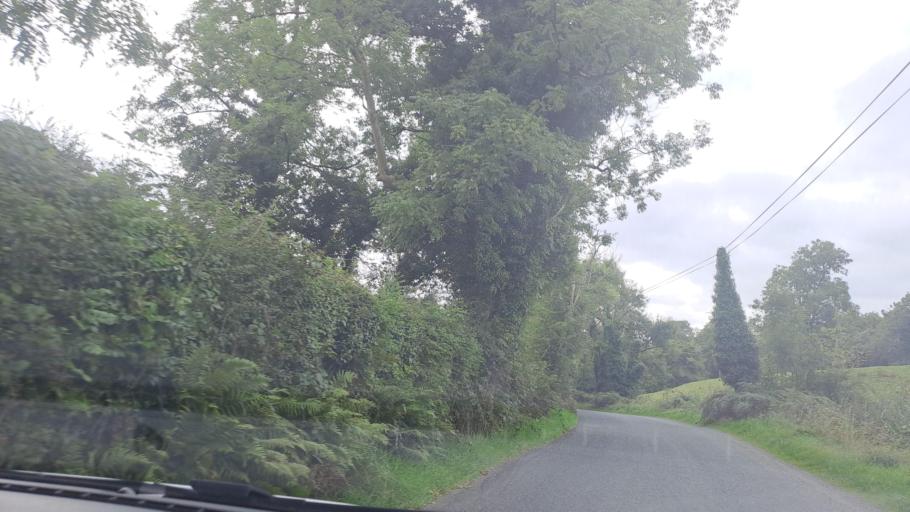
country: IE
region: Ulster
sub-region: An Cabhan
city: Bailieborough
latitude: 53.9371
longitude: -6.9185
